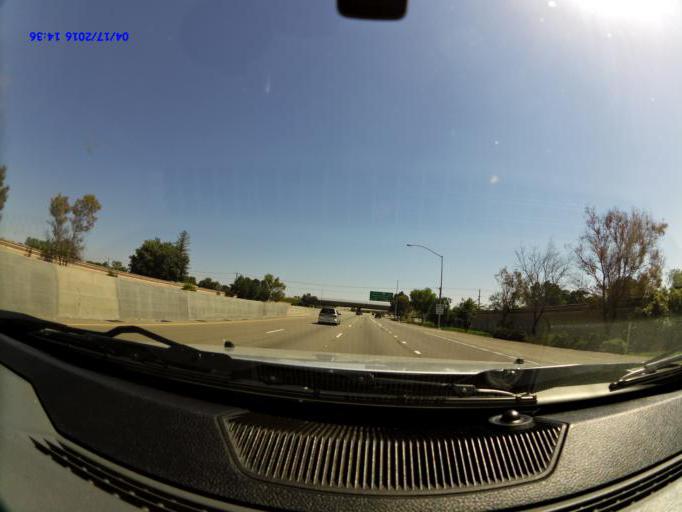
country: US
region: California
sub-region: San Joaquin County
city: Garden Acres
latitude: 37.9670
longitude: -121.2446
